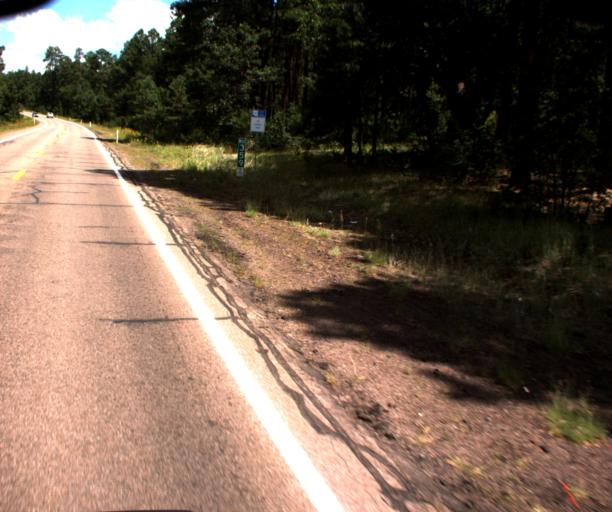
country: US
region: Arizona
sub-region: Navajo County
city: Pinetop-Lakeside
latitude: 34.0798
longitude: -109.8810
